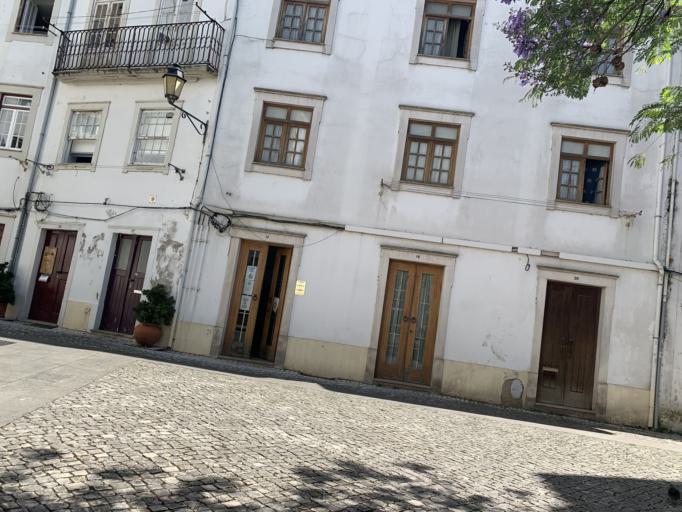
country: PT
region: Coimbra
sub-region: Coimbra
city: Coimbra
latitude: 40.2087
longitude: -8.4299
